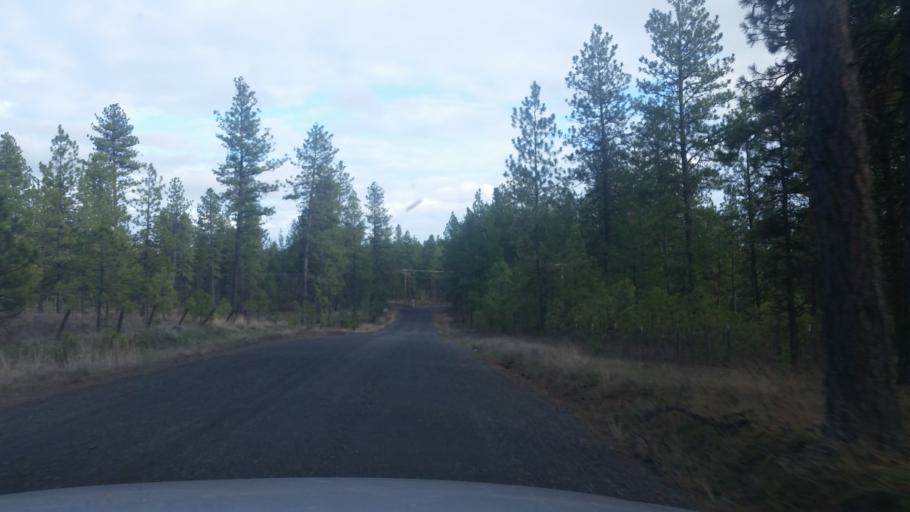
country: US
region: Washington
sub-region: Spokane County
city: Cheney
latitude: 47.4345
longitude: -117.4388
